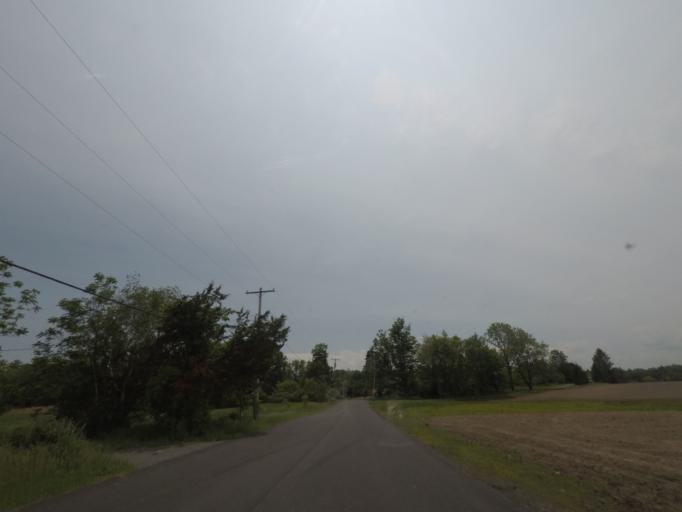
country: US
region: New York
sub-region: Rensselaer County
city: Castleton-on-Hudson
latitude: 42.5091
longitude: -73.7072
